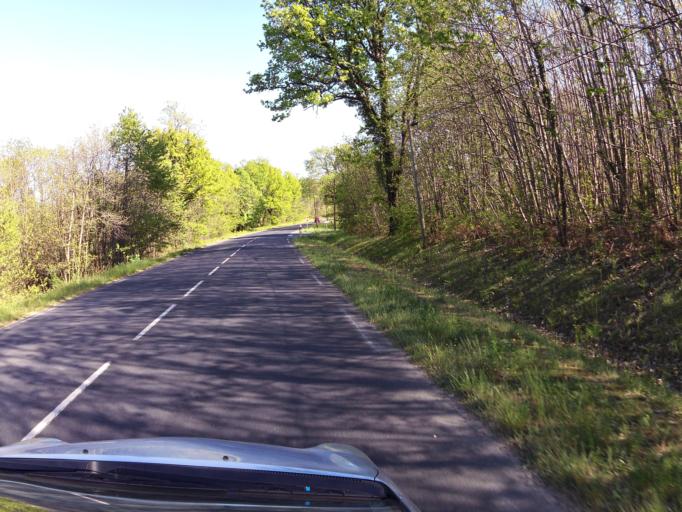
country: FR
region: Aquitaine
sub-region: Departement de la Dordogne
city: Montignac
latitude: 45.0208
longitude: 1.2333
